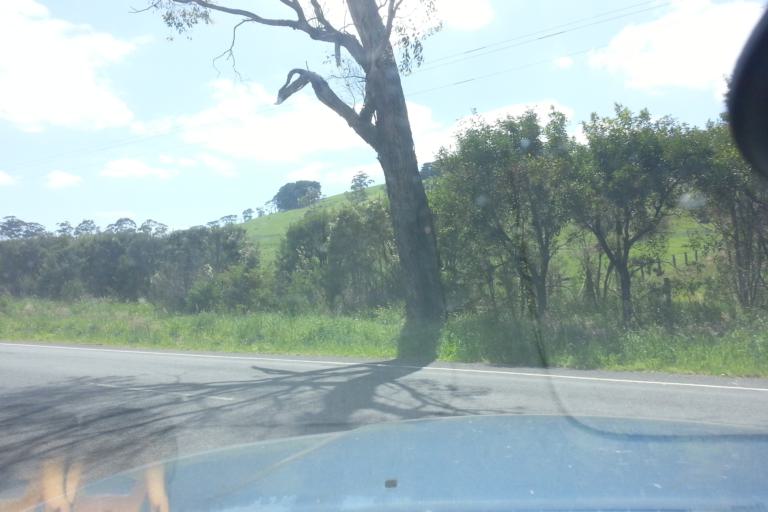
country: AU
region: Victoria
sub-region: Cardinia
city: Pakenham Upper
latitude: -38.0320
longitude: 145.4641
